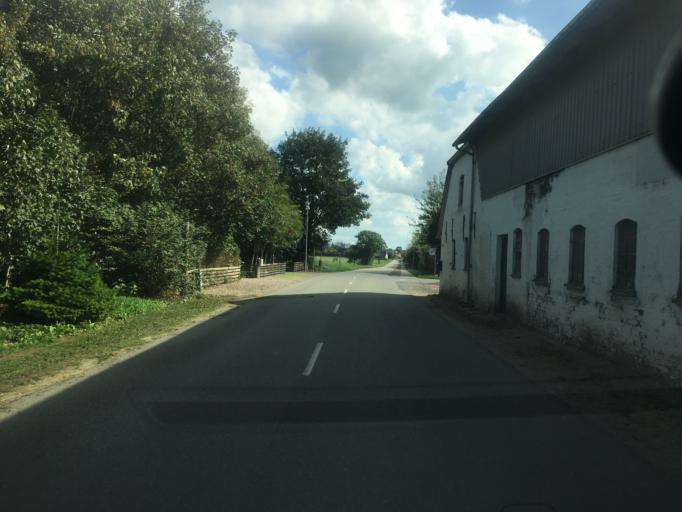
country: DE
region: Schleswig-Holstein
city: Ellhoft
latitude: 54.9467
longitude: 8.9658
